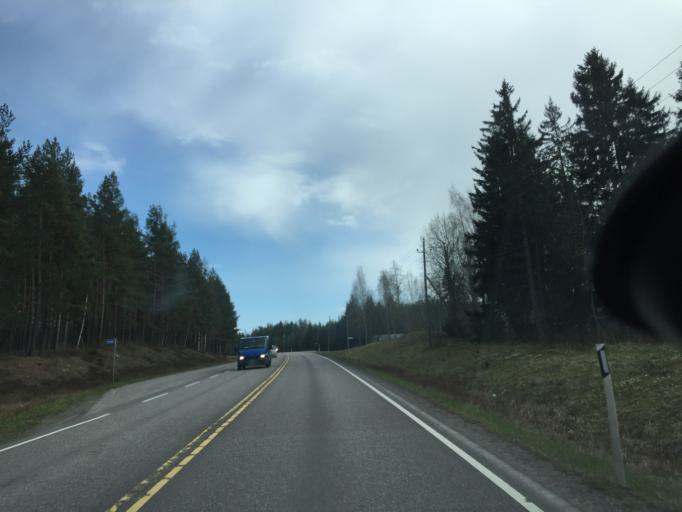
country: FI
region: Uusimaa
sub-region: Raaseporin
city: Ekenaes
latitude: 60.0442
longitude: 23.3359
